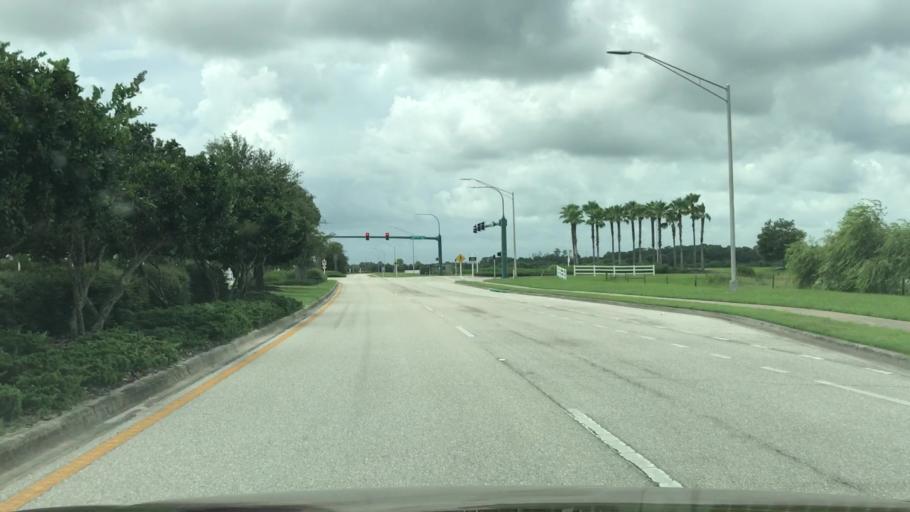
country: US
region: Florida
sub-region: Sarasota County
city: The Meadows
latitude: 27.4435
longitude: -82.4149
